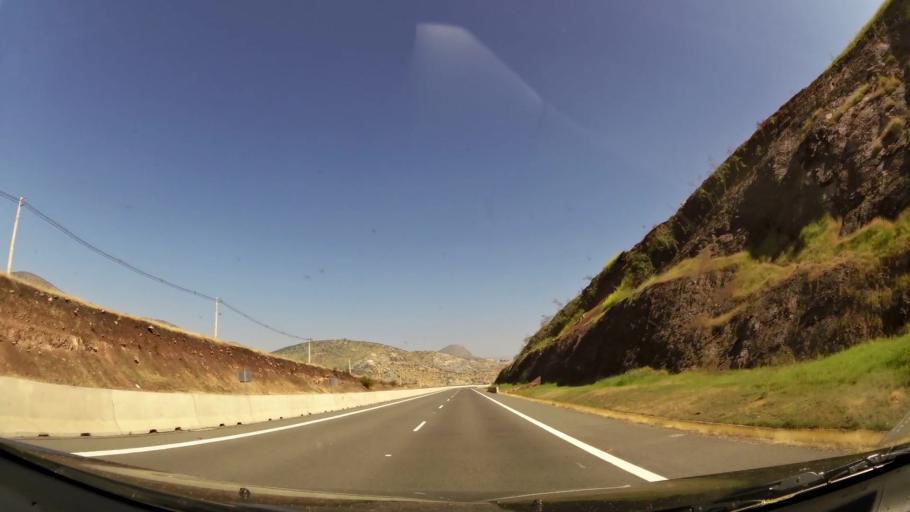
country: CL
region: Santiago Metropolitan
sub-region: Provincia de Chacabuco
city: Chicureo Abajo
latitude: -33.3125
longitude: -70.6461
